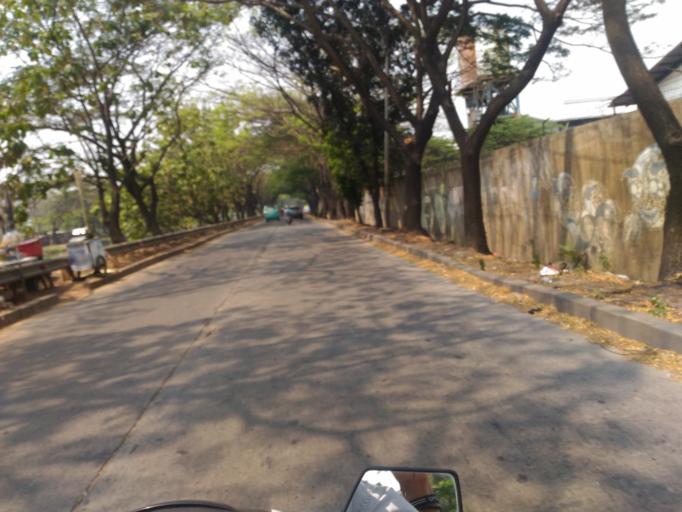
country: ID
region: Banten
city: Tangerang
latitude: -6.1593
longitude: 106.6118
